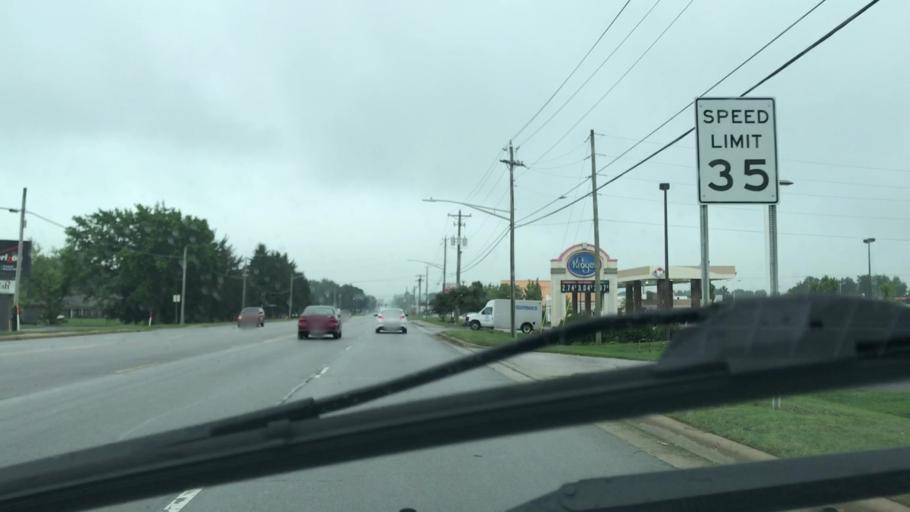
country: US
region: Indiana
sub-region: Boone County
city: Lebanon
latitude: 40.0702
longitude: -86.4738
